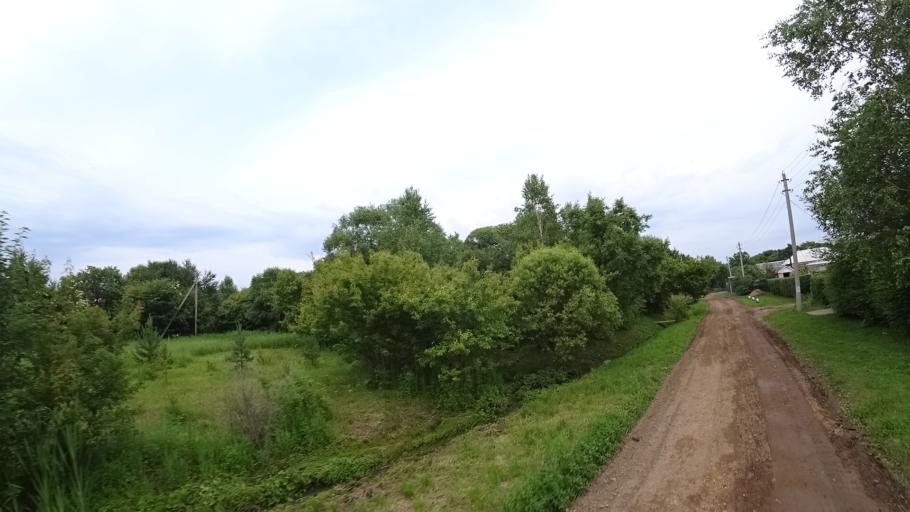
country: RU
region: Primorskiy
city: Novosysoyevka
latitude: 44.2405
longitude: 133.3775
